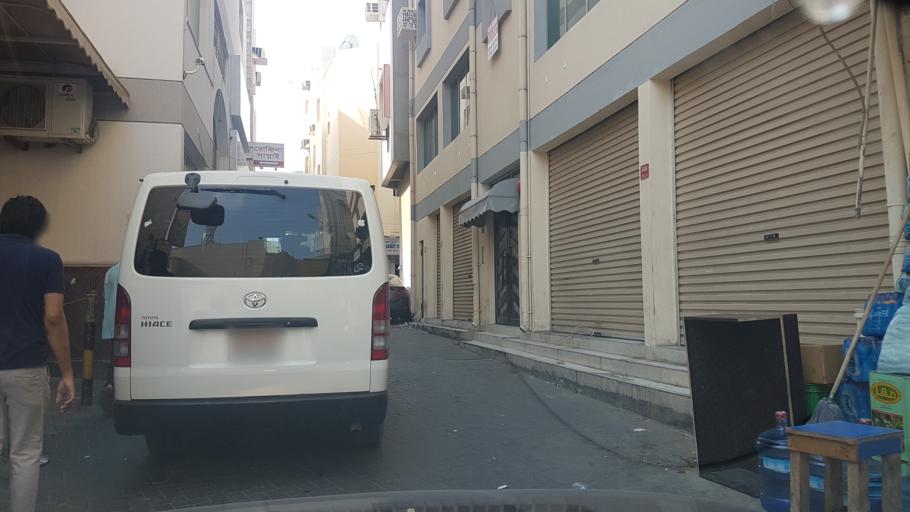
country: BH
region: Manama
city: Manama
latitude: 26.2294
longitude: 50.5748
